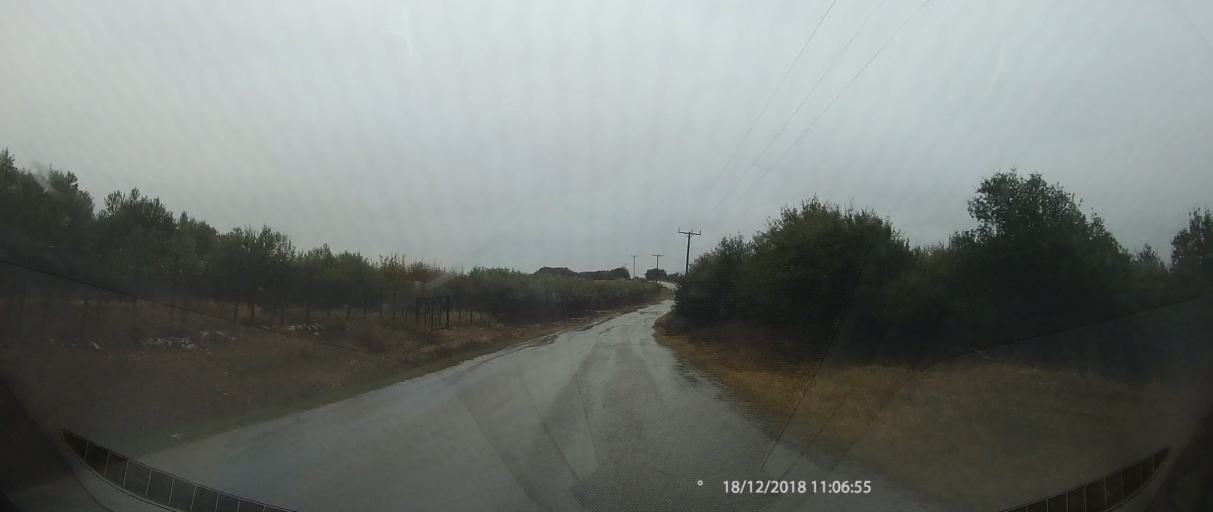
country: GR
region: Central Macedonia
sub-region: Nomos Pierias
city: Kato Milia
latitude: 40.2229
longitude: 22.3293
